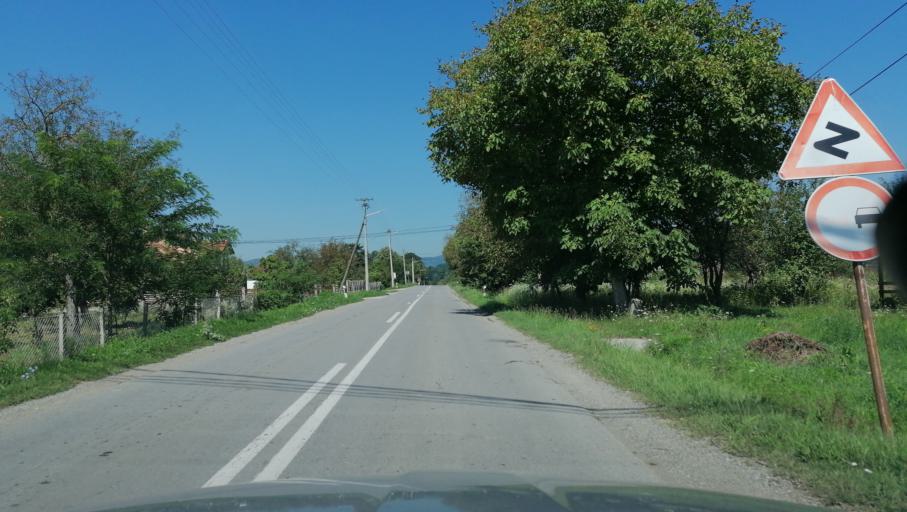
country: RS
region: Central Serbia
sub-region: Raski Okrug
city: Vrnjacka Banja
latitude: 43.7104
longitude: 20.8352
